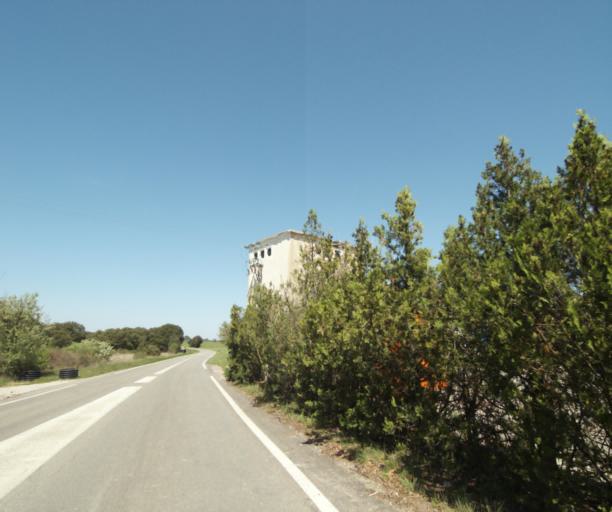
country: FR
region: Languedoc-Roussillon
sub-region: Departement de l'Herault
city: Beaulieu
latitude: 43.7283
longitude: 4.0094
